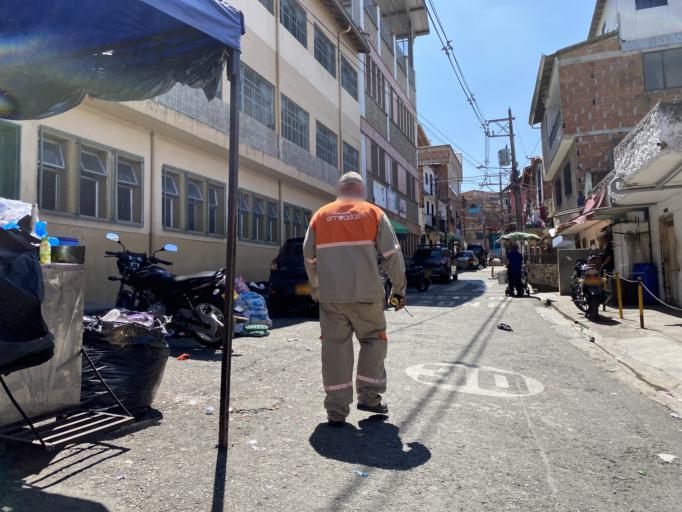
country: CO
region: Antioquia
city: Bello
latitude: 6.2989
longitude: -75.5495
